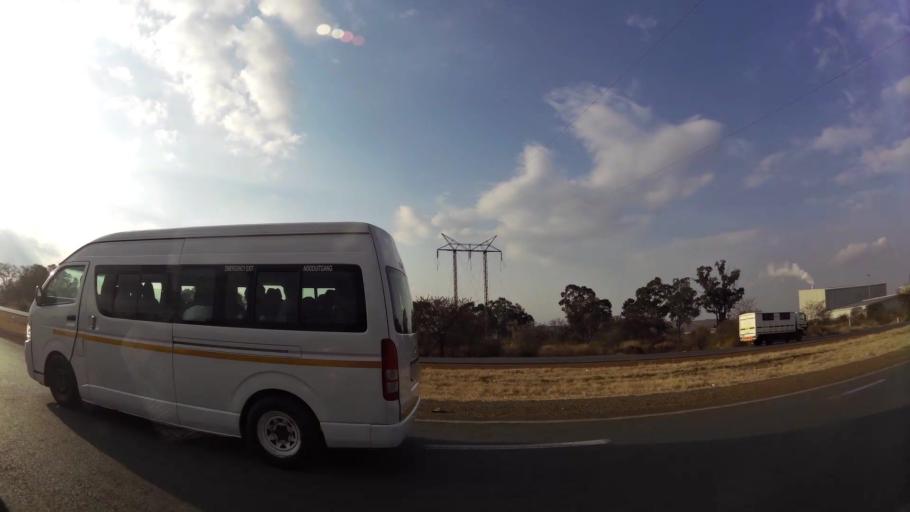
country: ZA
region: Gauteng
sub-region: Sedibeng District Municipality
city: Vereeniging
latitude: -26.6229
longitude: 27.8535
